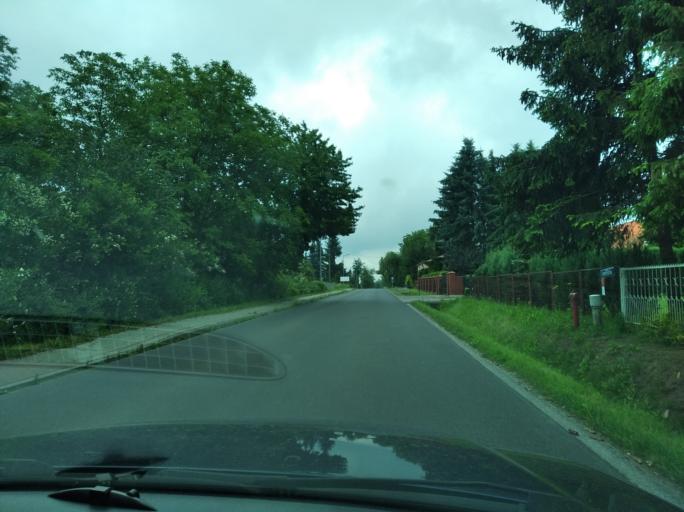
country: PL
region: Subcarpathian Voivodeship
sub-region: Powiat jaroslawski
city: Pawlosiow
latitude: 50.0227
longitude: 22.6386
